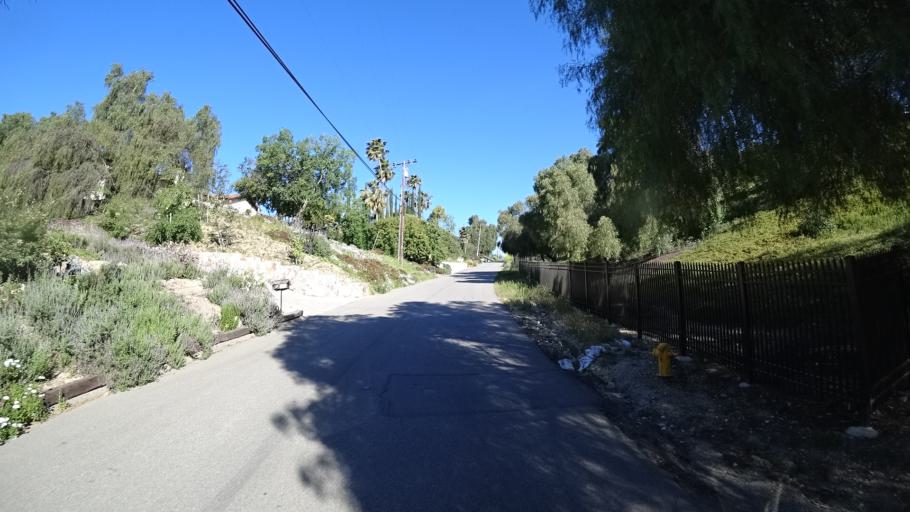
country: US
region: California
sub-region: Ventura County
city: Thousand Oaks
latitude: 34.1829
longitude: -118.8445
